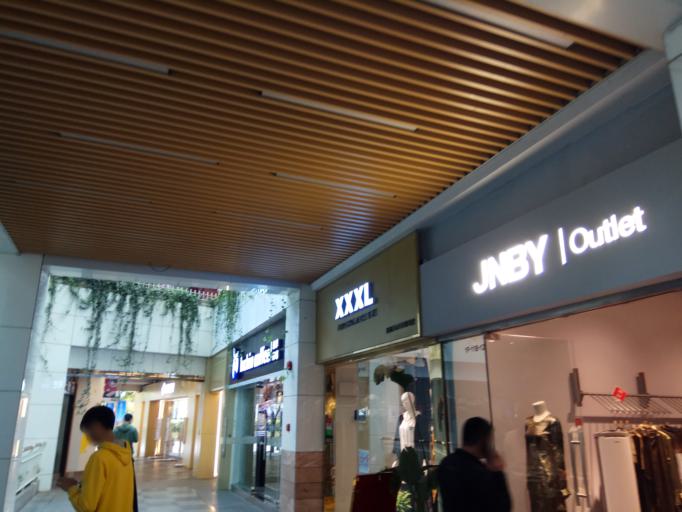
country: CN
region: Shanghai Shi
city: Changning
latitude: 31.2210
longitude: 121.4141
